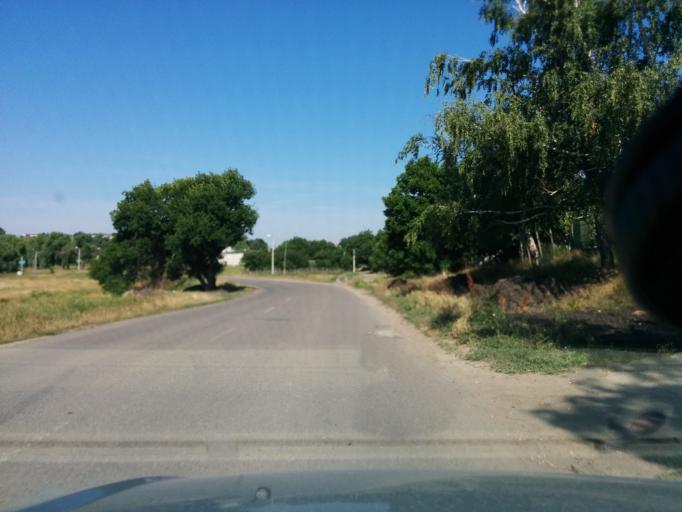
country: MD
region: Chisinau
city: Vadul lui Voda
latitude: 47.0659
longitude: 28.9869
